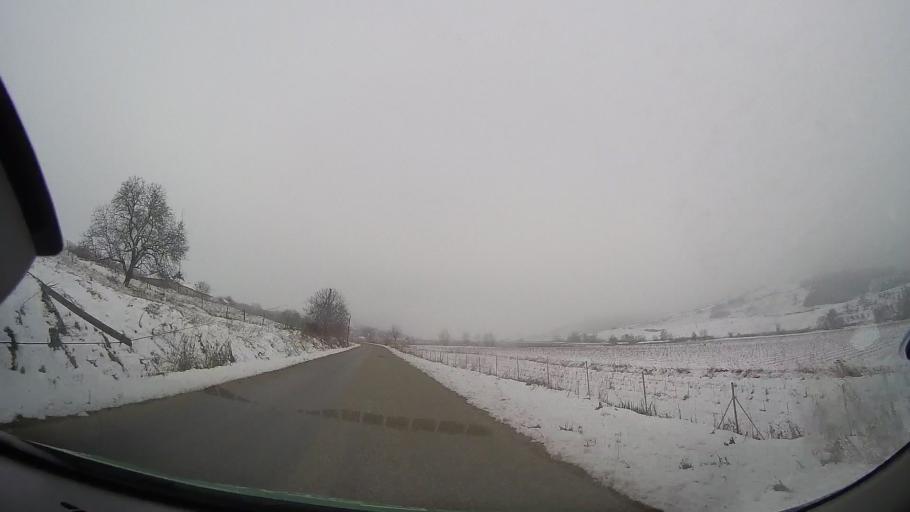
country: RO
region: Bacau
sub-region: Comuna Vultureni
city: Vultureni
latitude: 46.3630
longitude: 27.2863
